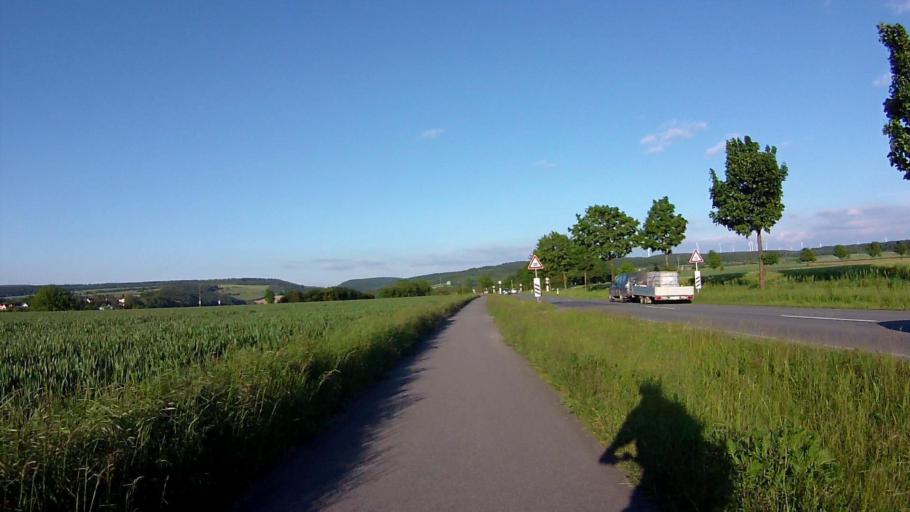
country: DE
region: North Rhine-Westphalia
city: Bad Lippspringe
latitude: 51.7422
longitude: 8.8379
